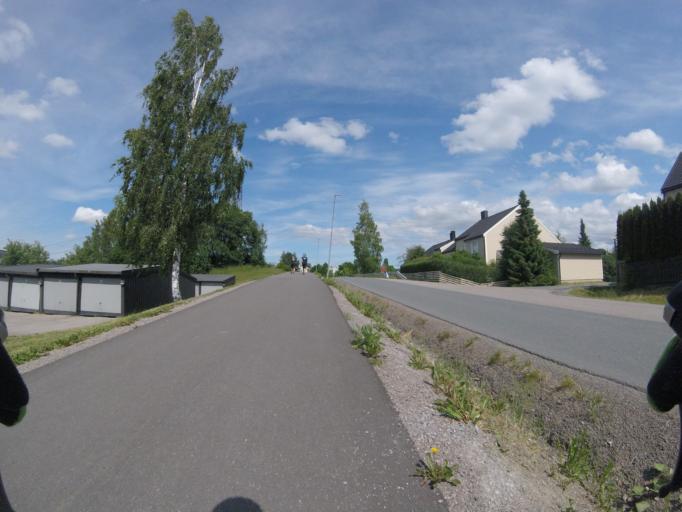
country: NO
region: Akershus
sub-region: Skedsmo
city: Lillestrom
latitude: 59.9885
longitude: 11.0366
